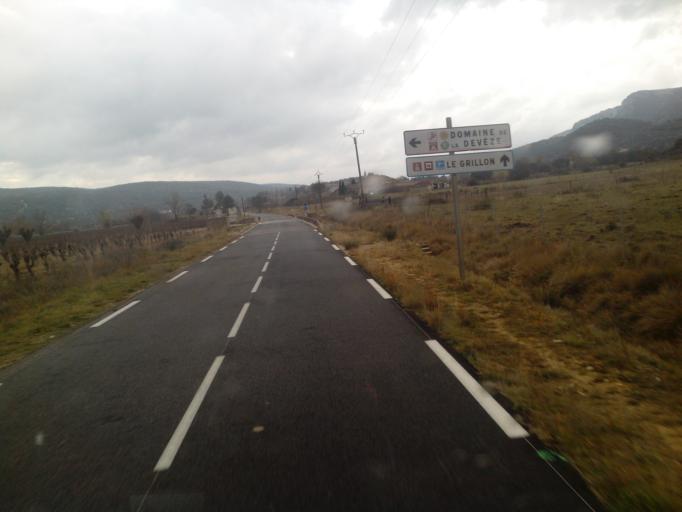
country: FR
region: Languedoc-Roussillon
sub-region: Departement du Gard
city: Saint-Hippolyte-du-Fort
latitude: 43.9341
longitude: 3.7990
